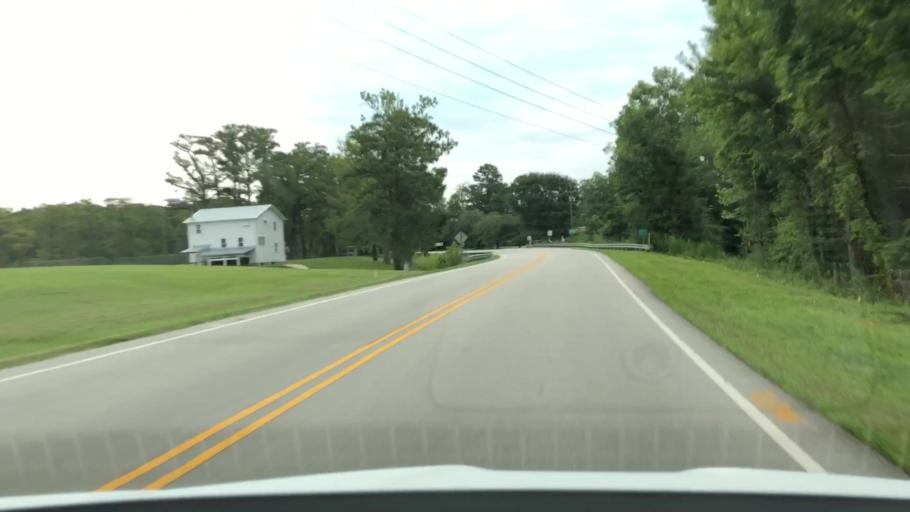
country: US
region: North Carolina
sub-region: Jones County
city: Trenton
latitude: 35.0589
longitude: -77.3562
